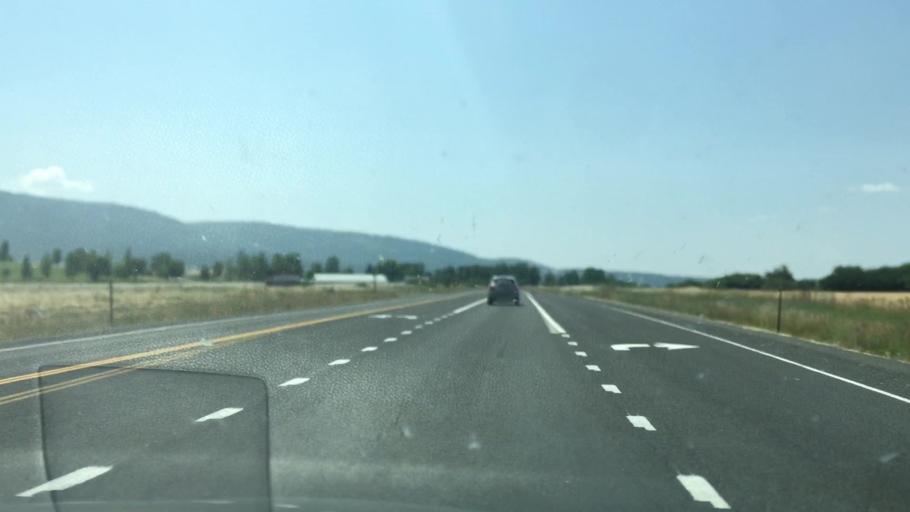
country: US
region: Idaho
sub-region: Idaho County
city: Grangeville
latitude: 45.9187
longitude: -116.1563
